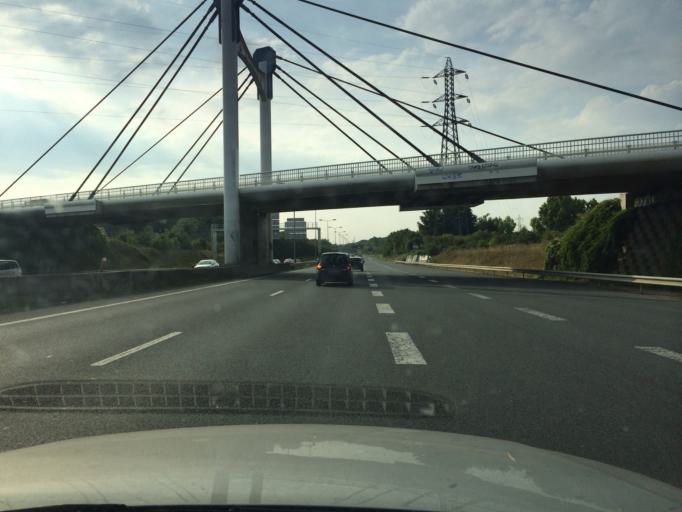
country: FR
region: Lower Normandy
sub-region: Departement du Calvados
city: Mondeville
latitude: 49.1715
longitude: -0.3055
